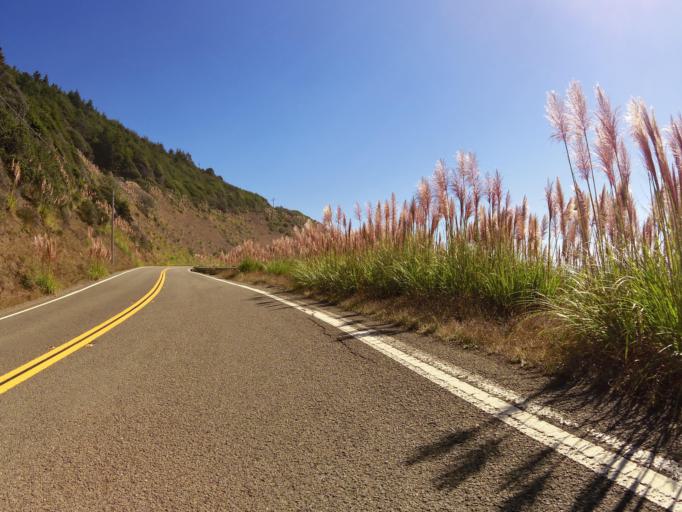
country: US
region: California
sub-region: Mendocino County
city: Fort Bragg
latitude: 39.6971
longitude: -123.7998
